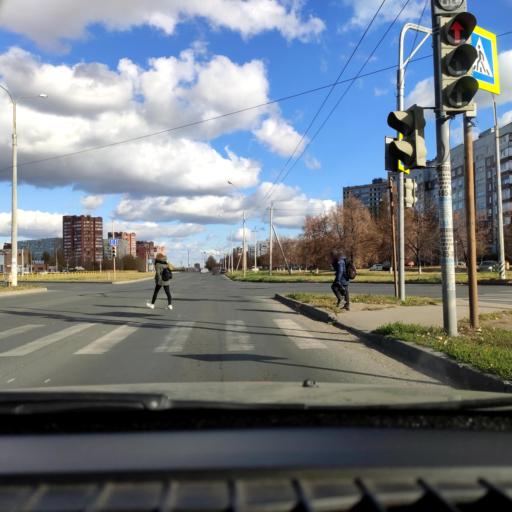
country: RU
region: Samara
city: Tol'yatti
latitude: 53.5418
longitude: 49.3153
